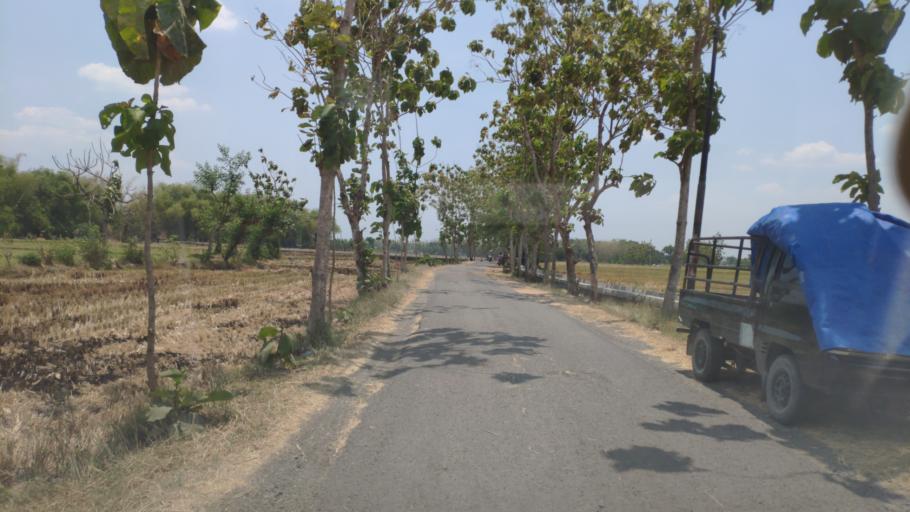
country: ID
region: Central Java
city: Klagen
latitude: -7.2138
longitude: 111.5392
